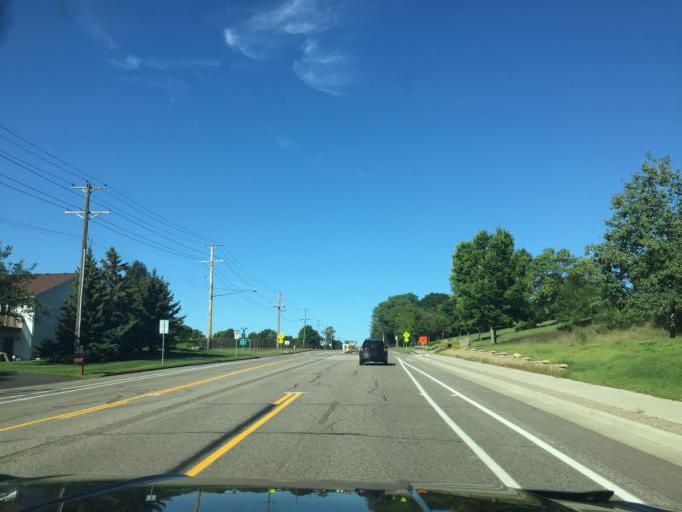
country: US
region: Minnesota
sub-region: Ramsey County
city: Roseville
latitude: 44.9918
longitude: -93.1201
